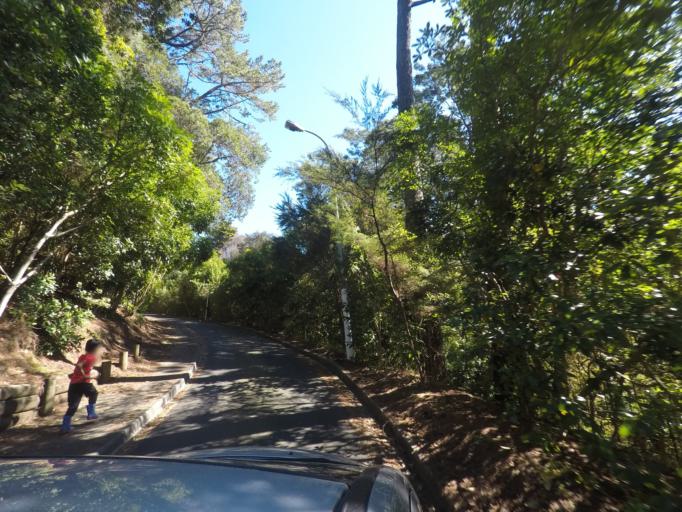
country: NZ
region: Auckland
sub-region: Auckland
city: Titirangi
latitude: -36.9316
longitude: 174.6988
